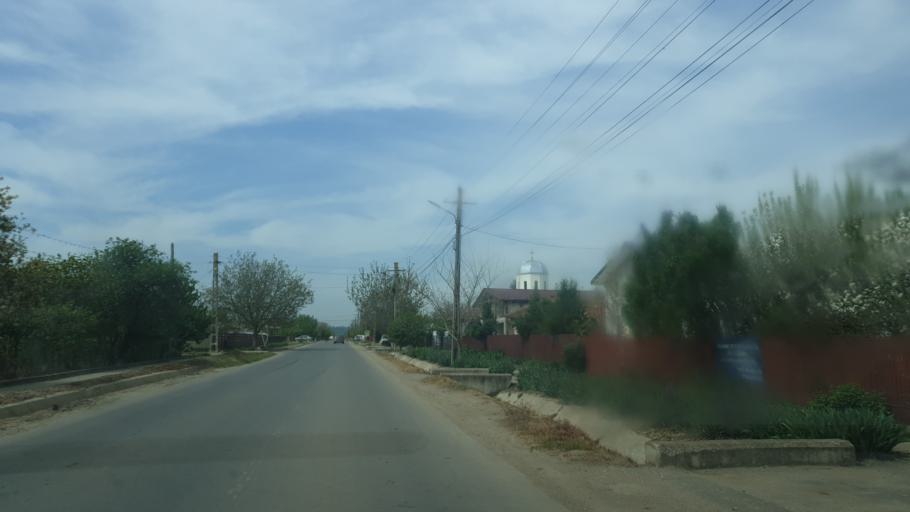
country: RO
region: Giurgiu
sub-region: Comuna Hotarele
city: Hotarele
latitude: 44.1831
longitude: 26.3995
